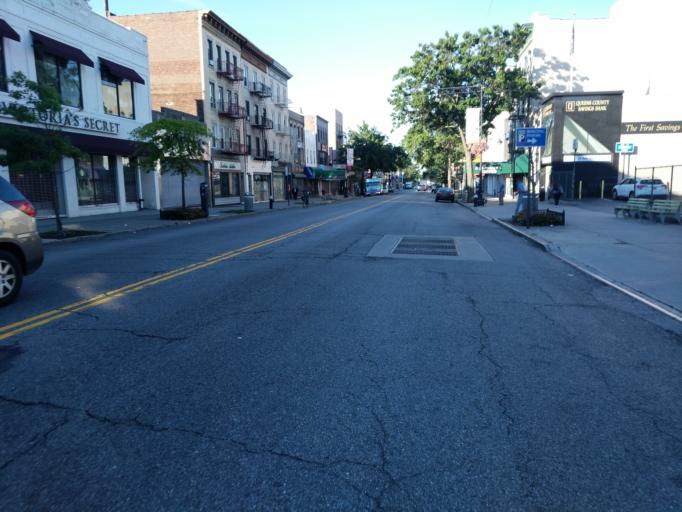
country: US
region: New York
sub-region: Queens County
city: Long Island City
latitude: 40.7606
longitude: -73.9176
